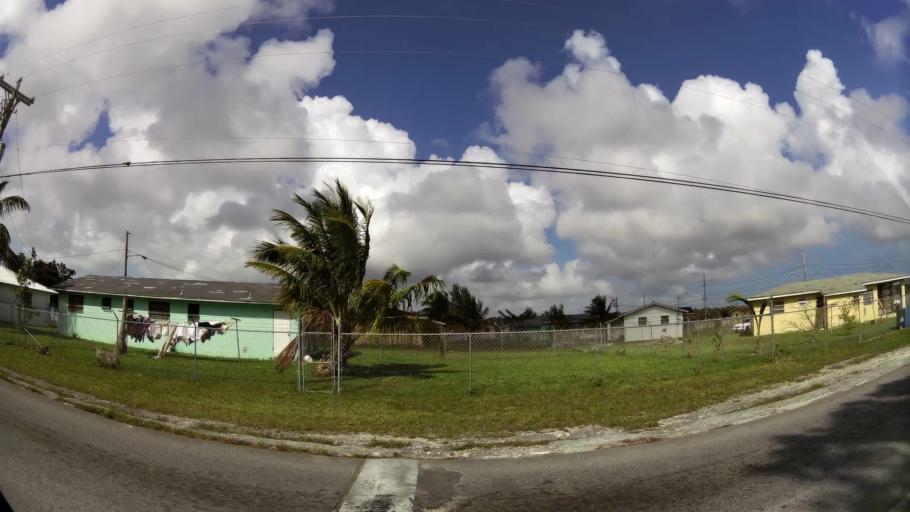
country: BS
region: Freeport
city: Lucaya
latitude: 26.5338
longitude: -78.6695
